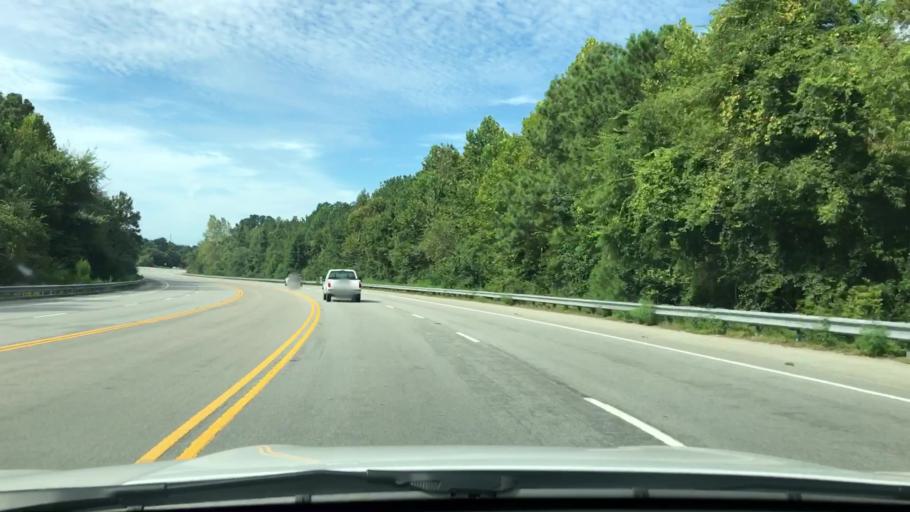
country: US
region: South Carolina
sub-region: Dorchester County
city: Summerville
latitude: 33.0146
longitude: -80.1733
